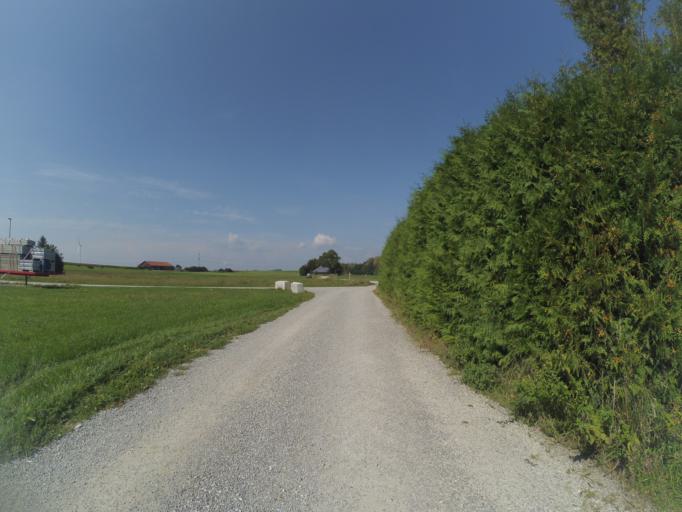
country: DE
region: Bavaria
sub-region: Swabia
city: Lamerdingen
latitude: 48.1092
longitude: 10.7730
